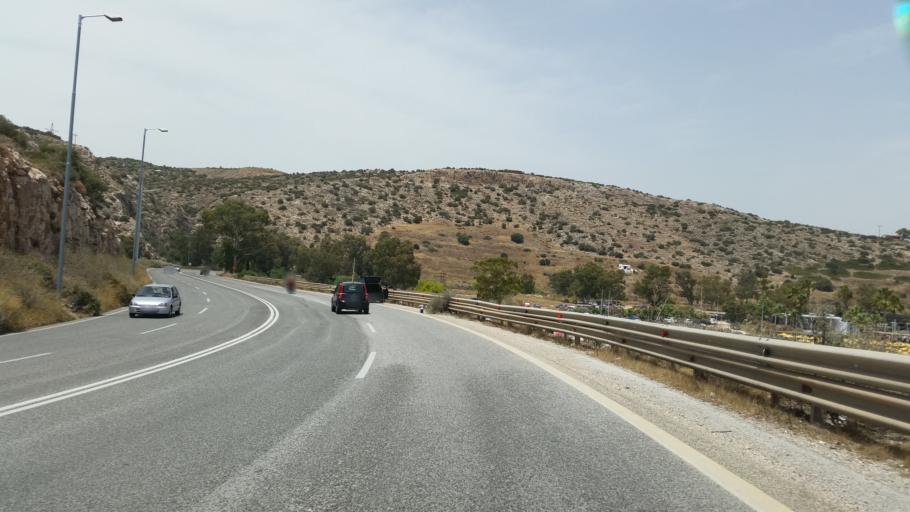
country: GR
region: Attica
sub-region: Nomarchia Anatolikis Attikis
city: Agia Marina
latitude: 37.8173
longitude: 23.8345
